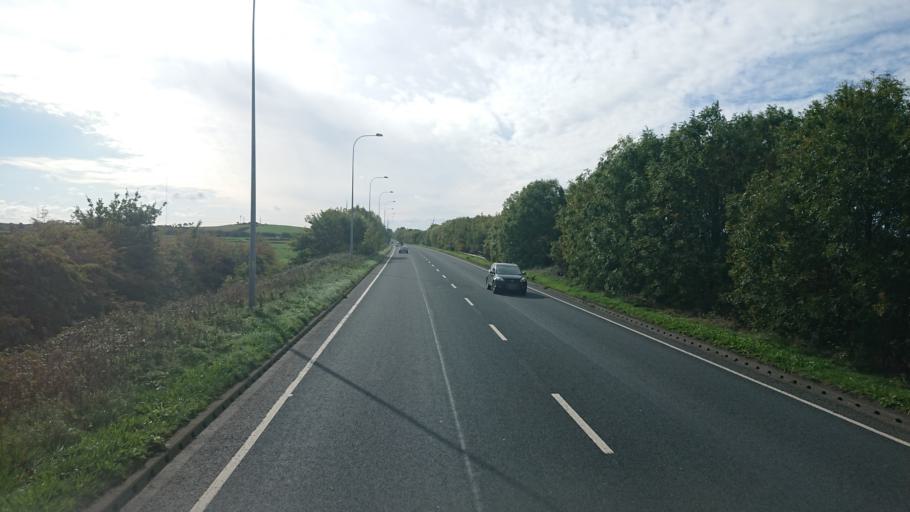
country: GB
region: England
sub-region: Lancashire
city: Morecambe
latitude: 54.0498
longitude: -2.8468
